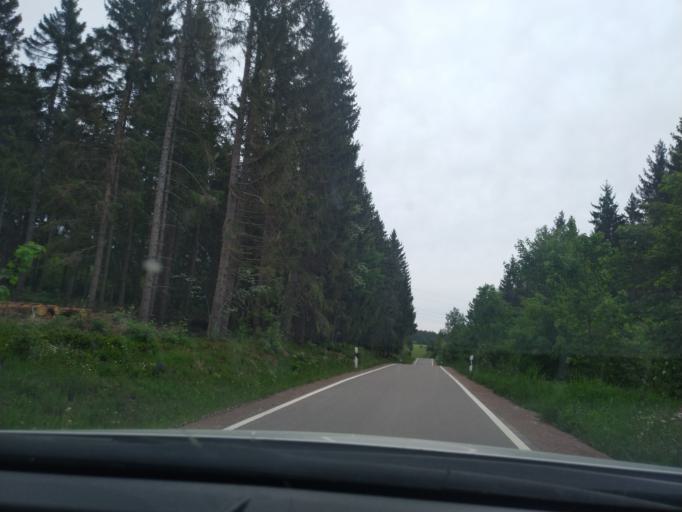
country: DE
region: Baden-Wuerttemberg
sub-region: Freiburg Region
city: Schluchsee
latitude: 47.8063
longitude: 8.2222
